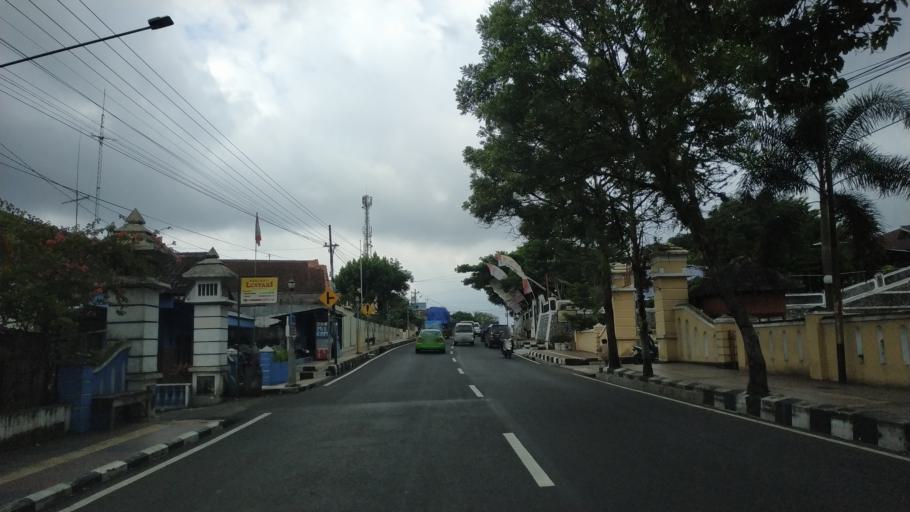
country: ID
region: Central Java
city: Magelang
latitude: -7.2905
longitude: 110.1310
